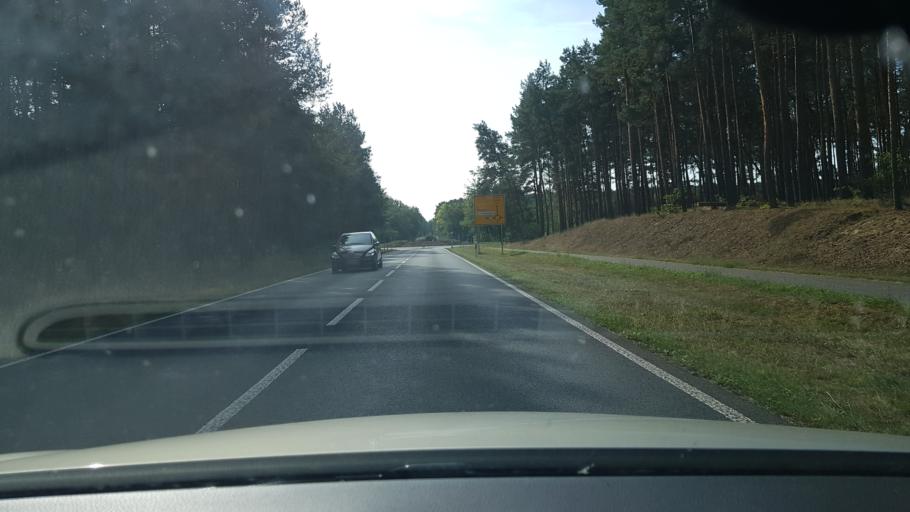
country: DE
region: Brandenburg
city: Lawitz
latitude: 52.1249
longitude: 14.6410
